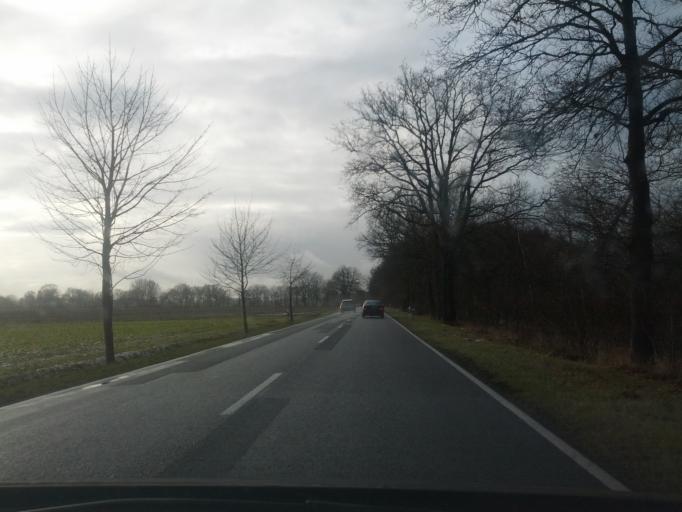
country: DE
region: Lower Saxony
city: Lengenbostel
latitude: 53.3230
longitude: 9.5235
